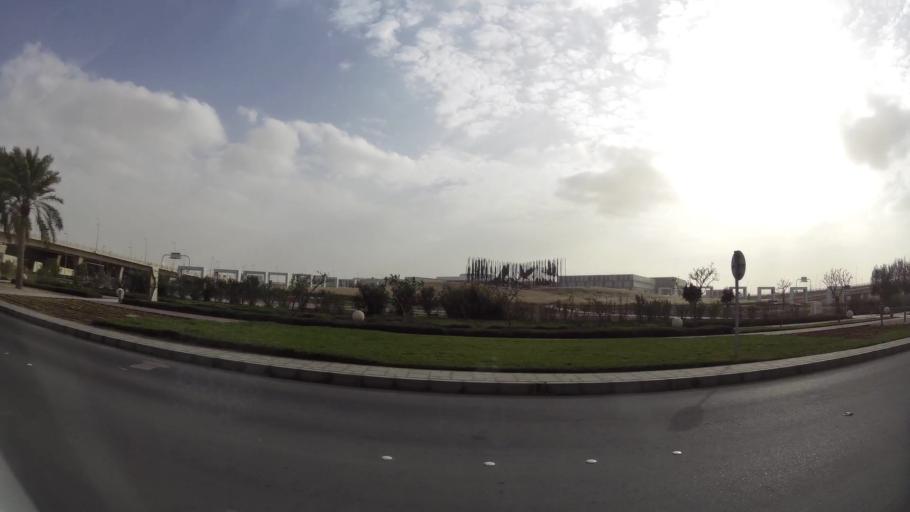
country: AE
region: Abu Dhabi
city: Abu Dhabi
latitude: 24.4937
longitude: 54.6111
